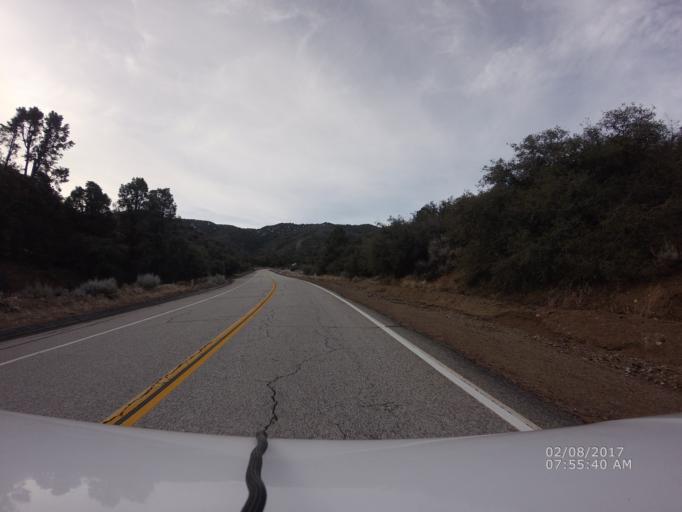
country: US
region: California
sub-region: San Bernardino County
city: Pinon Hills
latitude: 34.4149
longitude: -117.7693
